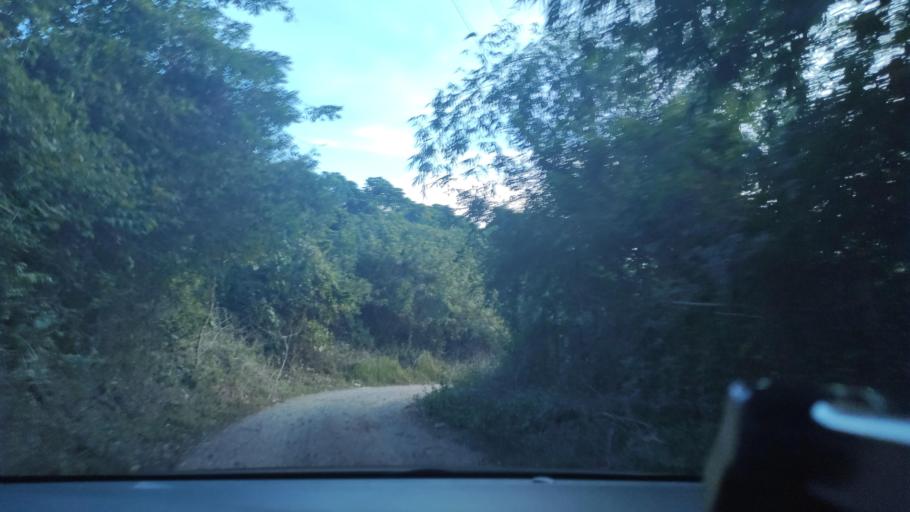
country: PH
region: Ilocos
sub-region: Province of Pangasinan
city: Balingasay
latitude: 16.3089
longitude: 119.8629
